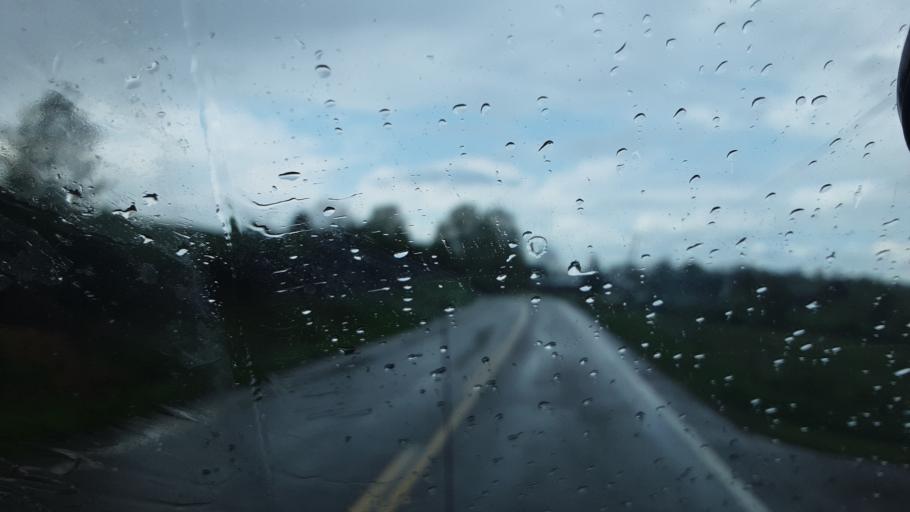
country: US
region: Ohio
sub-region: Muskingum County
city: New Concord
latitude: 40.0340
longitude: -81.7572
